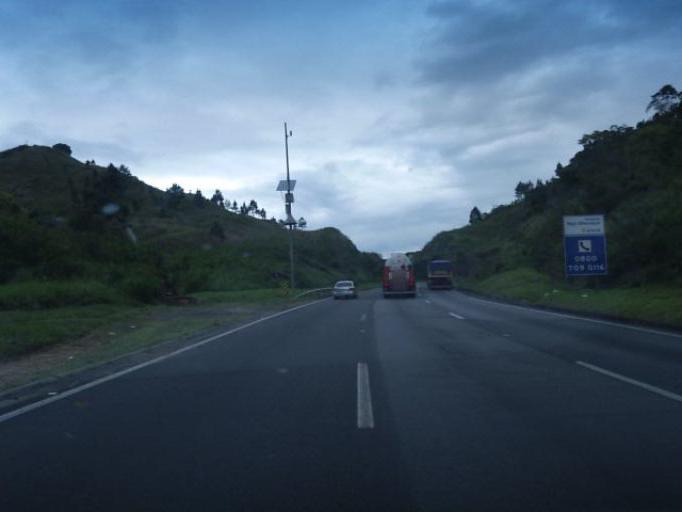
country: BR
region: Sao Paulo
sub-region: Cajati
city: Cajati
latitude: -24.9674
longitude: -48.4897
